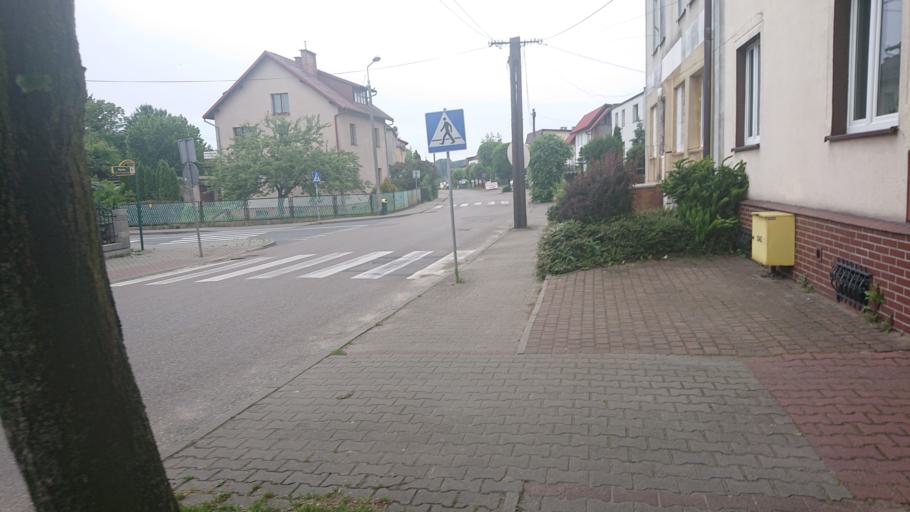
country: PL
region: Pomeranian Voivodeship
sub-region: Powiat chojnicki
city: Chojnice
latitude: 53.6989
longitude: 17.5652
